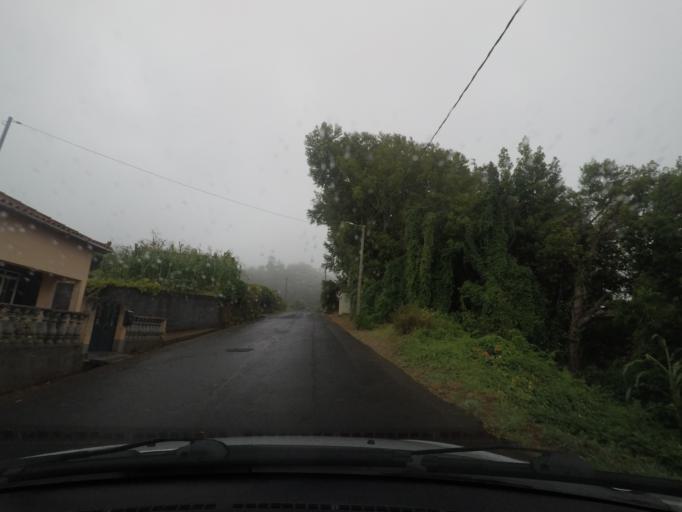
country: PT
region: Madeira
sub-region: Santana
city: Santana
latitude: 32.7952
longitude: -16.8715
